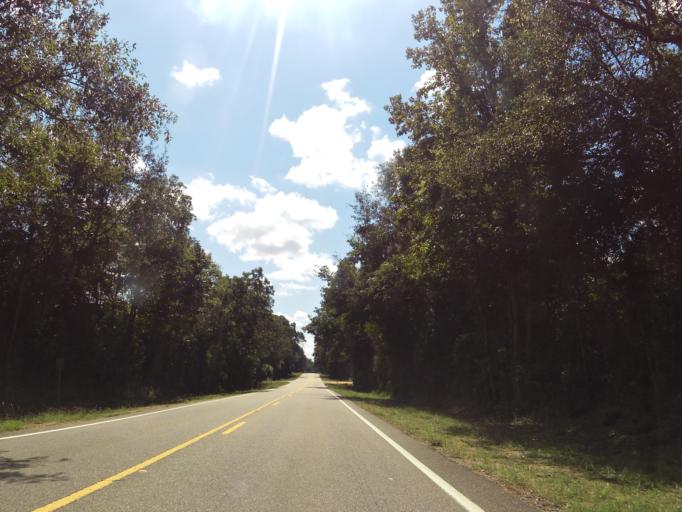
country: US
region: Alabama
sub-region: Dallas County
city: Selma
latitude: 32.4816
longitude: -87.0927
